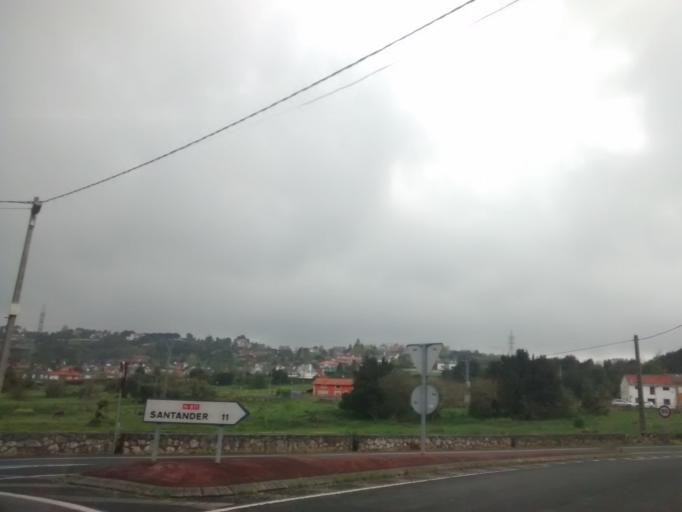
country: ES
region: Cantabria
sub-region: Provincia de Cantabria
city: Santa Cruz de Bezana
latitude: 43.4100
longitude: -3.9406
